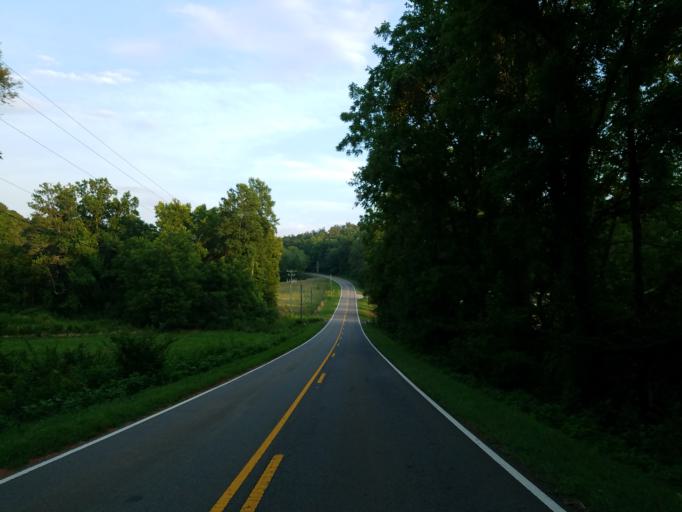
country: US
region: Georgia
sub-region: Pickens County
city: Jasper
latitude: 34.5304
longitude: -84.4780
